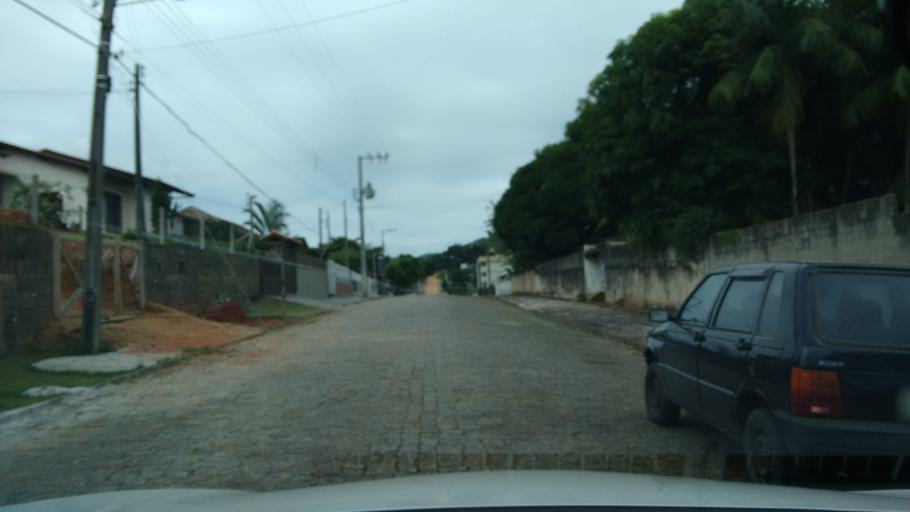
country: BR
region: Santa Catarina
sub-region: Timbo
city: Timbo
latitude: -26.8120
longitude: -49.2680
